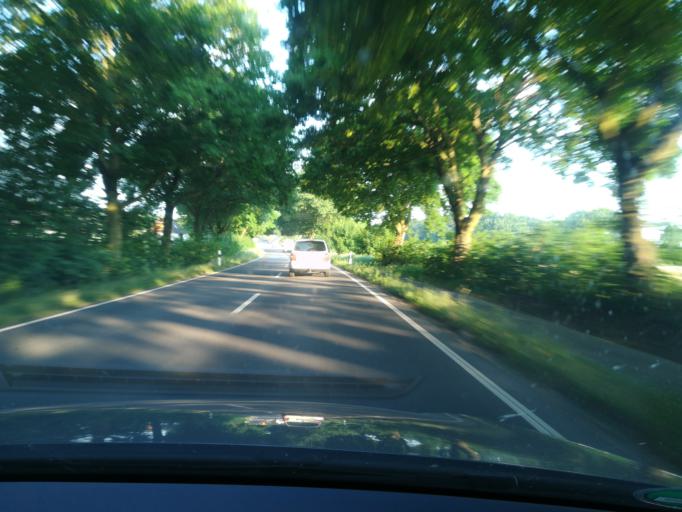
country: DE
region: Schleswig-Holstein
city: Siek
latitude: 53.6322
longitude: 10.3147
